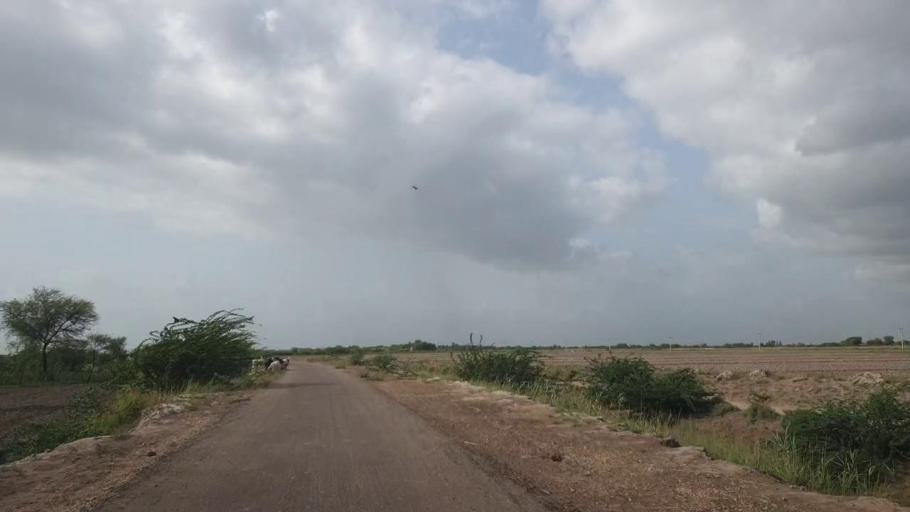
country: PK
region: Sindh
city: Kadhan
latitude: 24.5645
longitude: 69.0639
